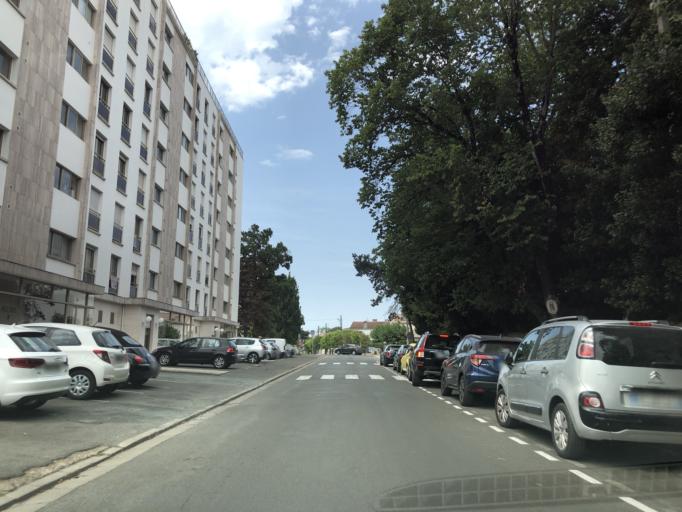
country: FR
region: Poitou-Charentes
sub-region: Departement de la Charente-Maritime
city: Royan
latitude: 45.6240
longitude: -1.0359
